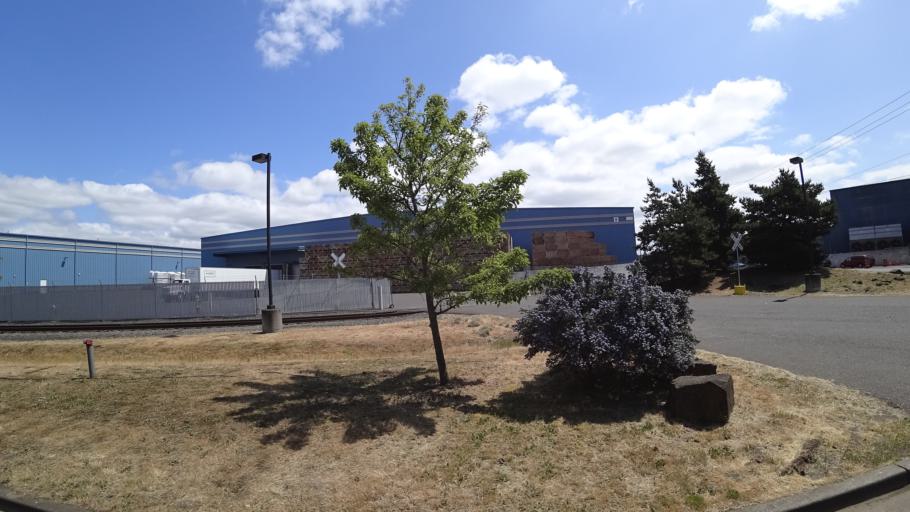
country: US
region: Washington
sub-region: Clark County
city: Vancouver
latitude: 45.6336
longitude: -122.6916
